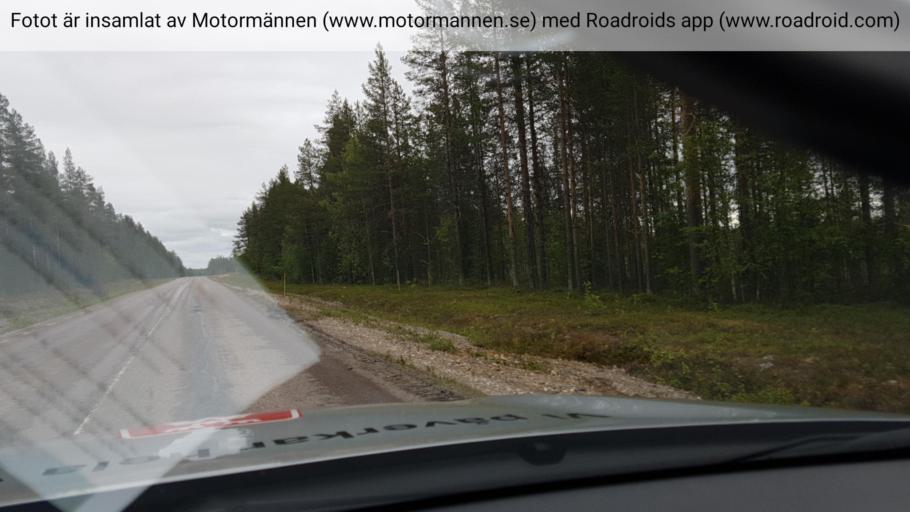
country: SE
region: Norrbotten
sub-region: Overkalix Kommun
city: OEverkalix
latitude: 67.0639
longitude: 22.2683
